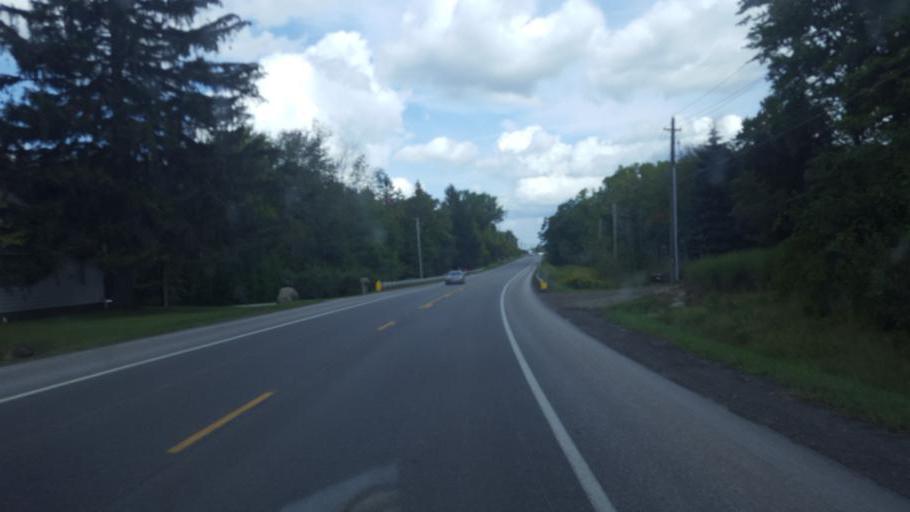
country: US
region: Ohio
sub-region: Geauga County
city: Middlefield
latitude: 41.4303
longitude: -81.0598
